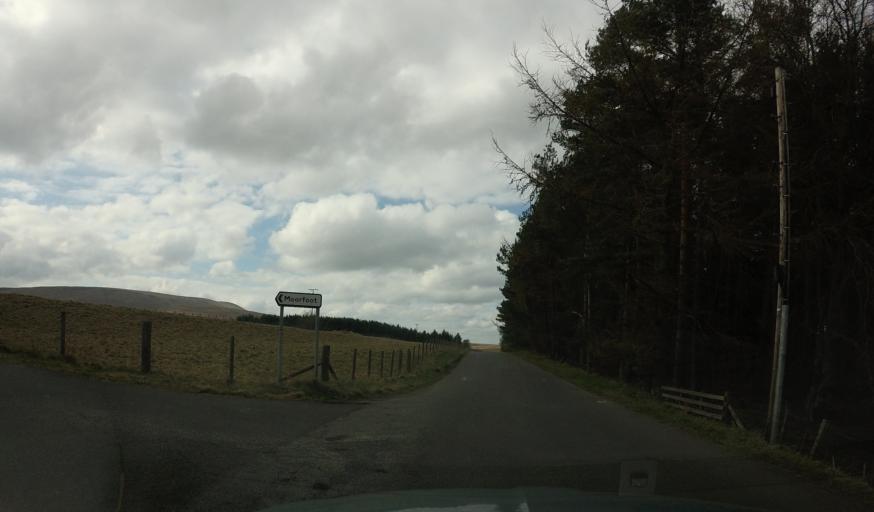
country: GB
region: Scotland
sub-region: Midlothian
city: Penicuik
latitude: 55.7666
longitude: -3.1412
